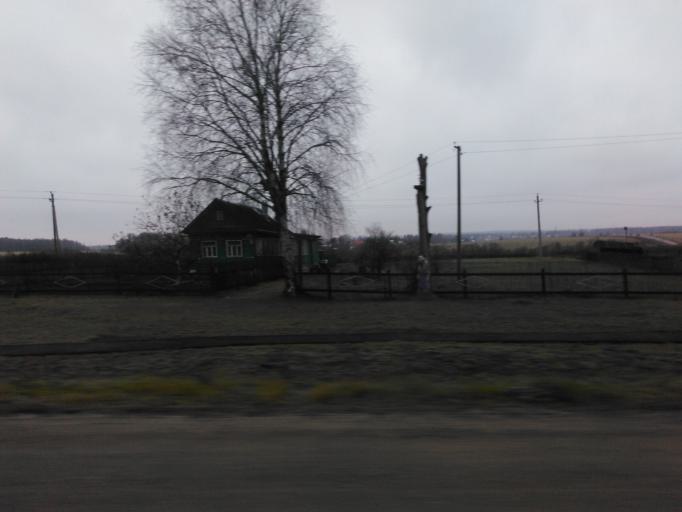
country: RU
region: Moskovskaya
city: Ashukino
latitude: 56.1520
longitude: 37.9880
